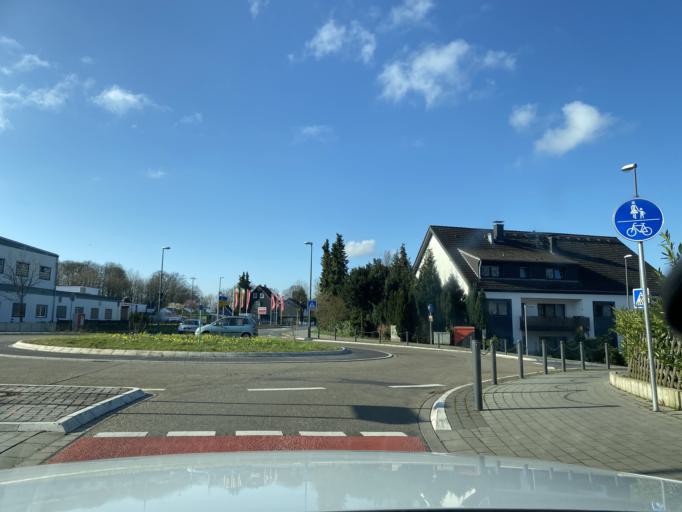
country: DE
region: North Rhine-Westphalia
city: Burscheid
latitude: 51.0993
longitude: 7.1528
